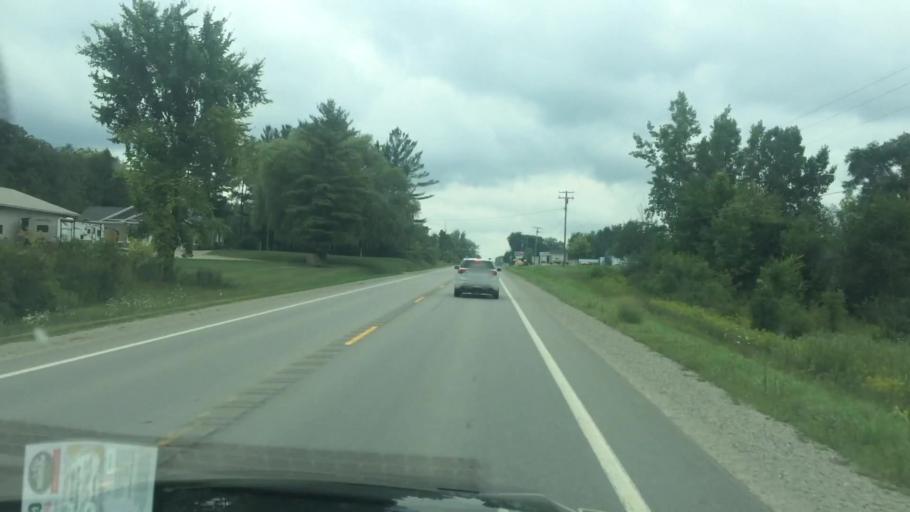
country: US
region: Michigan
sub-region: Tuscola County
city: Cass City
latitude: 43.5964
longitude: -83.0966
